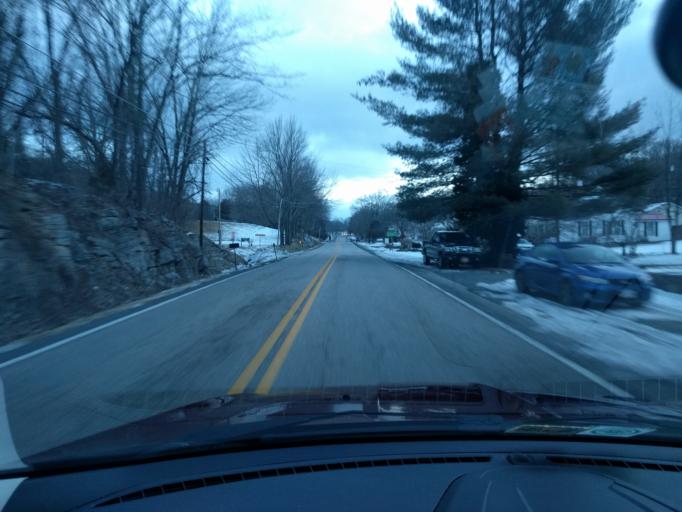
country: US
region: Virginia
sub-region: Bath County
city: Warm Springs
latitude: 37.9711
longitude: -79.8514
